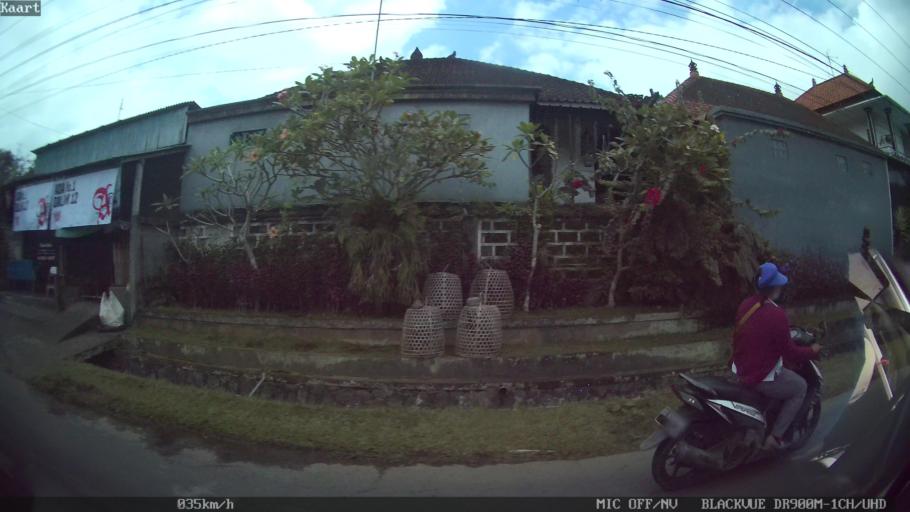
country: ID
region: Bali
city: Bangli
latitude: -8.4546
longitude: 115.3843
